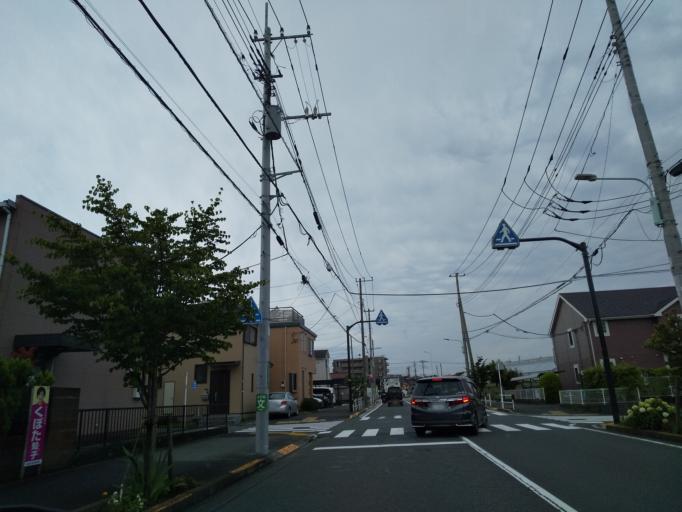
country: JP
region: Tokyo
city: Hino
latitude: 35.6815
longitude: 139.3789
